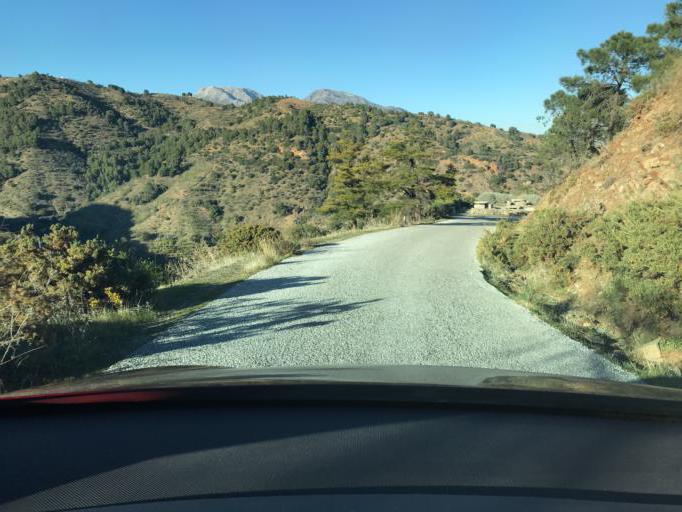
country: ES
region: Andalusia
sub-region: Provincia de Malaga
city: Tolox
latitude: 36.6850
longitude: -4.9125
